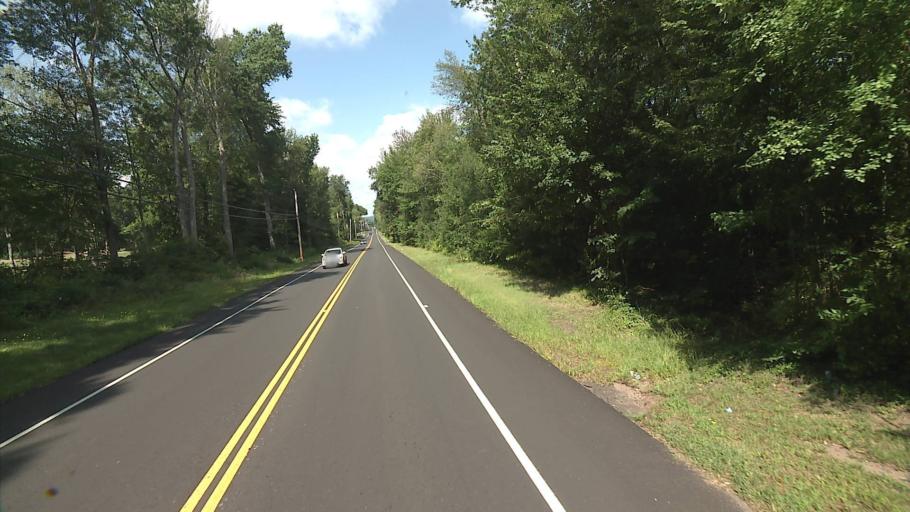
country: US
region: Connecticut
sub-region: Hartford County
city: Blue Hills
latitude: 41.7997
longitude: -72.7305
